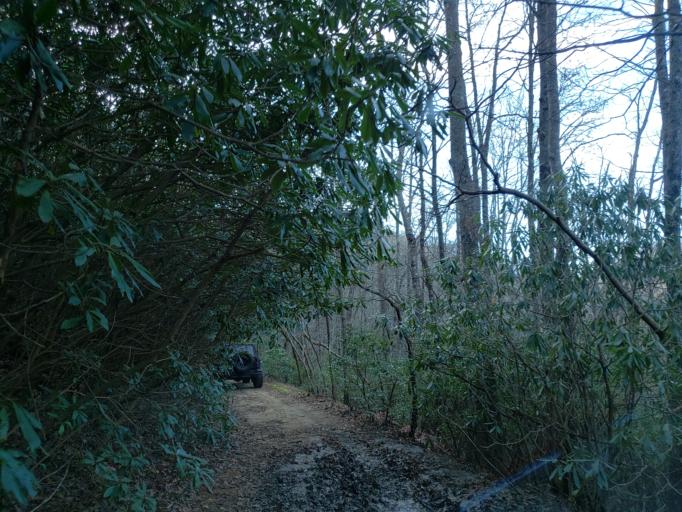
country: US
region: Georgia
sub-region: Lumpkin County
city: Dahlonega
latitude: 34.6626
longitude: -84.1082
